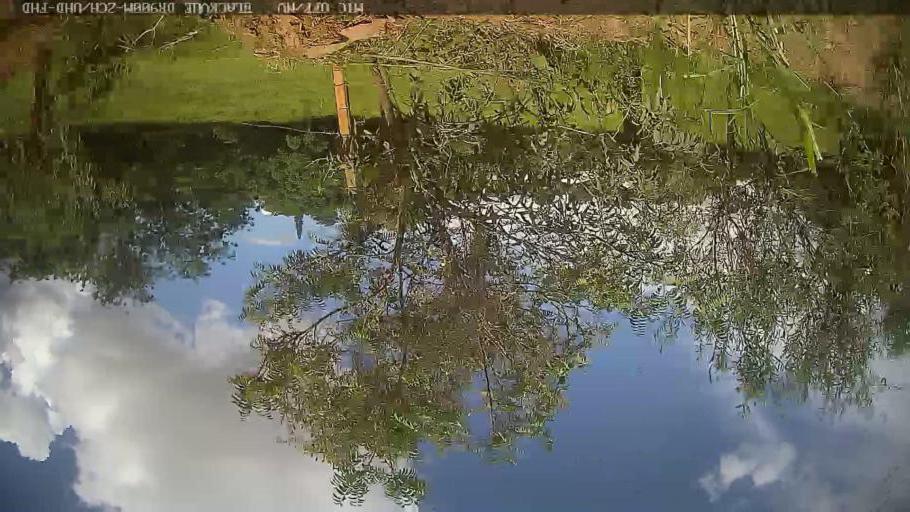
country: BR
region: Sao Paulo
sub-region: Bom Jesus Dos Perdoes
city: Bom Jesus dos Perdoes
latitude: -23.1183
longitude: -46.4928
